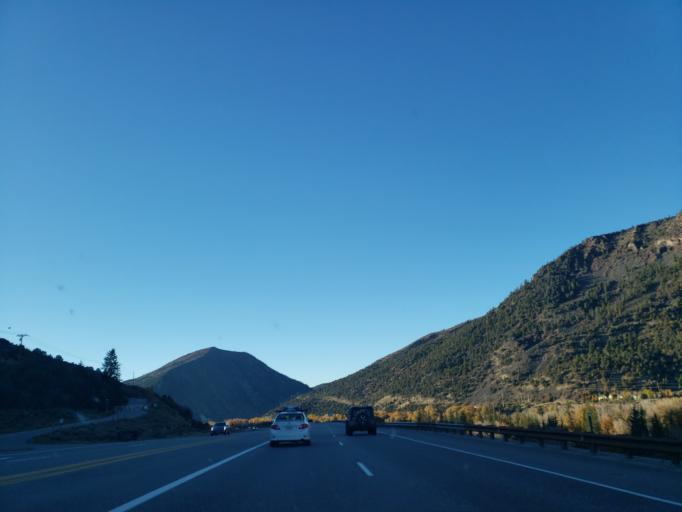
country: US
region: Colorado
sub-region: Pitkin County
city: Snowmass Village
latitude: 39.2895
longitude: -106.9102
